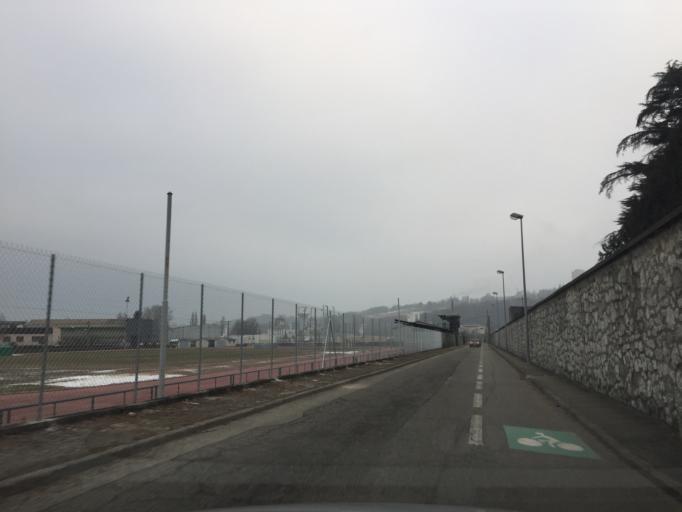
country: FR
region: Rhone-Alpes
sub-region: Departement de la Savoie
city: Cognin
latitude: 45.5765
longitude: 5.9046
